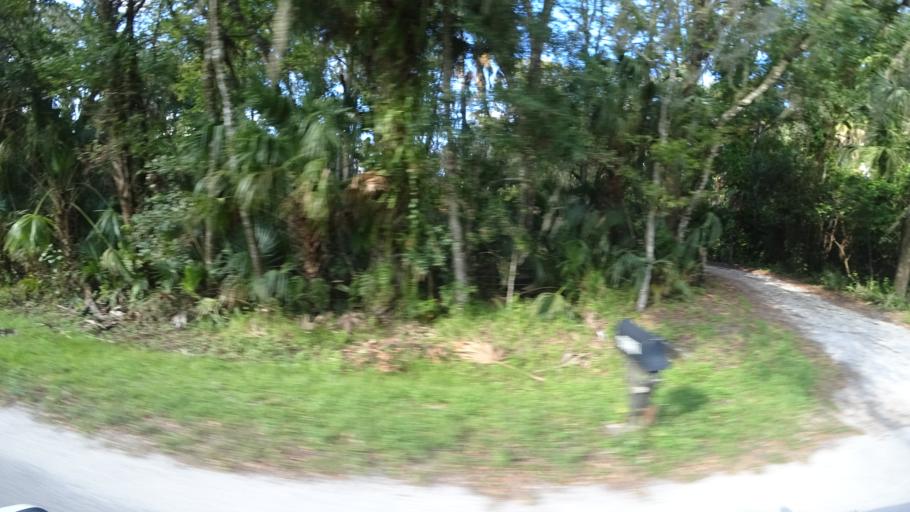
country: US
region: Florida
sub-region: Manatee County
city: Ellenton
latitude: 27.4829
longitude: -82.4722
